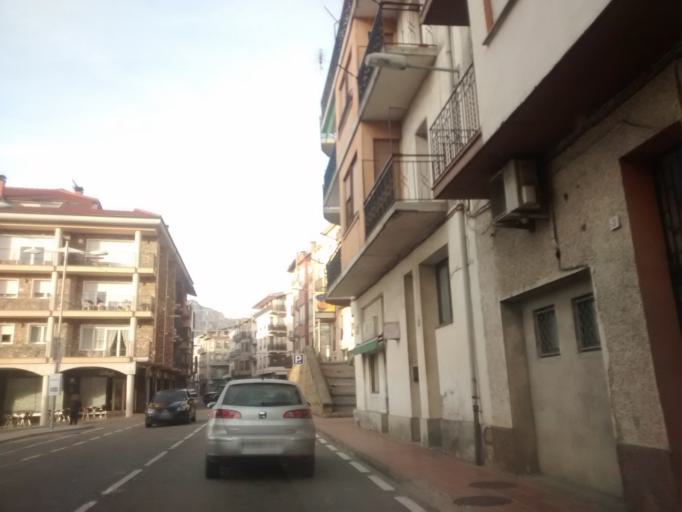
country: ES
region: Catalonia
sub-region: Provincia de Lleida
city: Oliana
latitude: 42.0661
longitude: 1.3139
